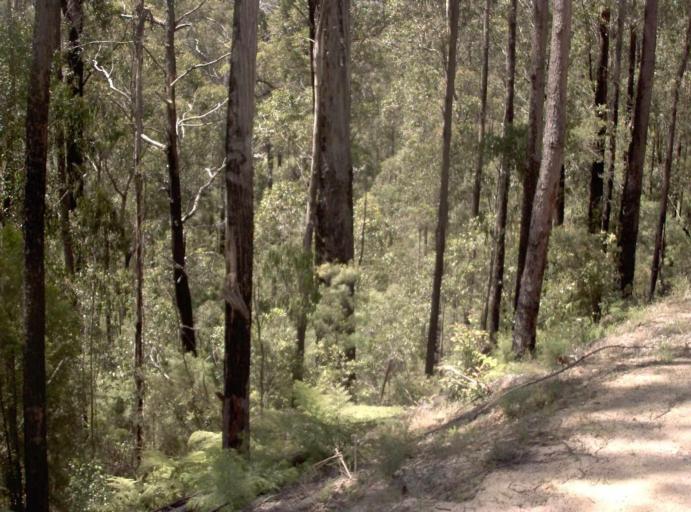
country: AU
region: New South Wales
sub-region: Bombala
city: Bombala
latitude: -37.5925
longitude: 148.9770
